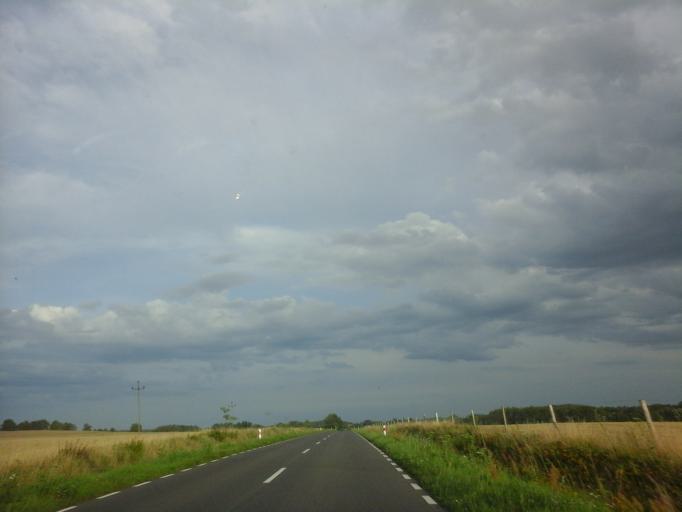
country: PL
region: West Pomeranian Voivodeship
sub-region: Powiat kamienski
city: Golczewo
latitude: 53.8593
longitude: 14.9259
